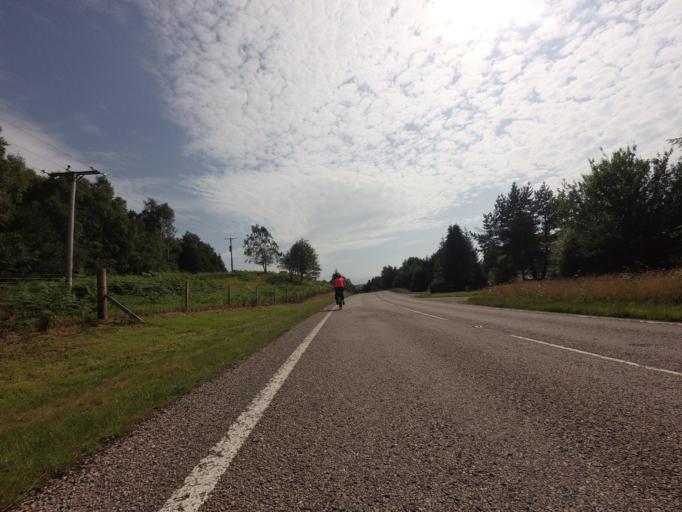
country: GB
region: Scotland
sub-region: Highland
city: Evanton
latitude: 57.9272
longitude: -4.4005
